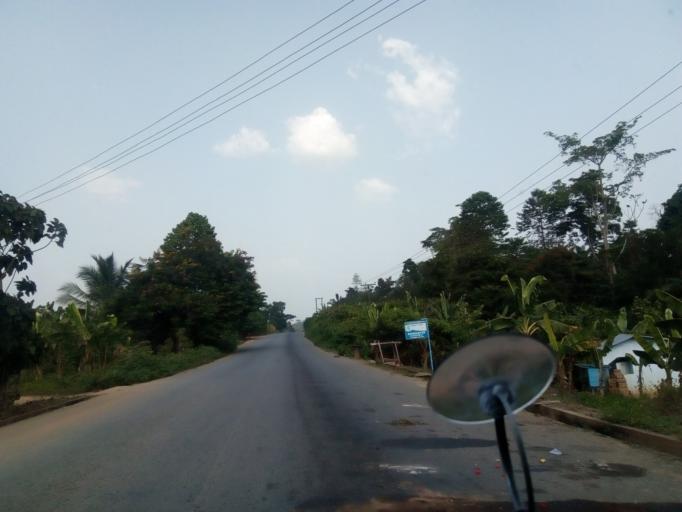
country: GH
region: Eastern
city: Suhum
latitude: 6.0470
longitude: -0.4115
